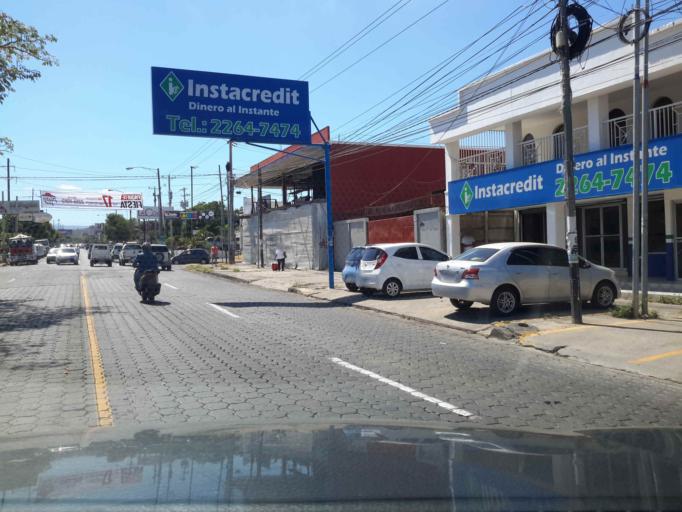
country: NI
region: Managua
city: Ciudad Sandino
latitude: 12.1505
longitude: -86.3046
